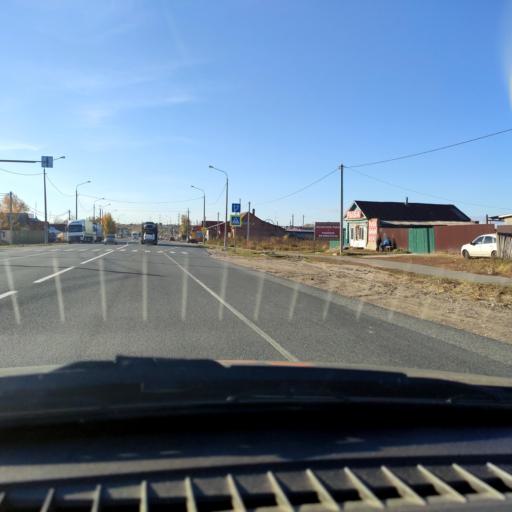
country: RU
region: Samara
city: Mezhdurechensk
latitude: 53.2481
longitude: 49.1785
